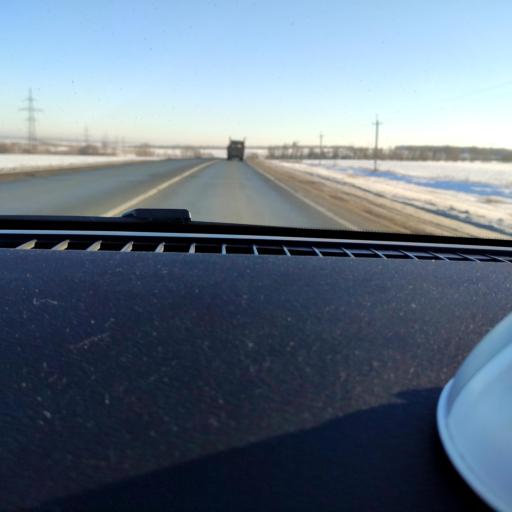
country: RU
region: Samara
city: Smyshlyayevka
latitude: 53.1480
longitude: 50.4987
